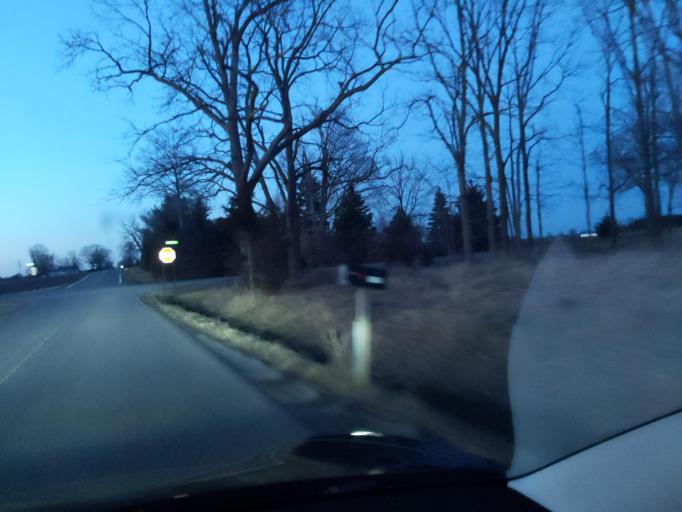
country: US
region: Michigan
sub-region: Ingham County
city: Stockbridge
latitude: 42.5348
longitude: -84.2209
